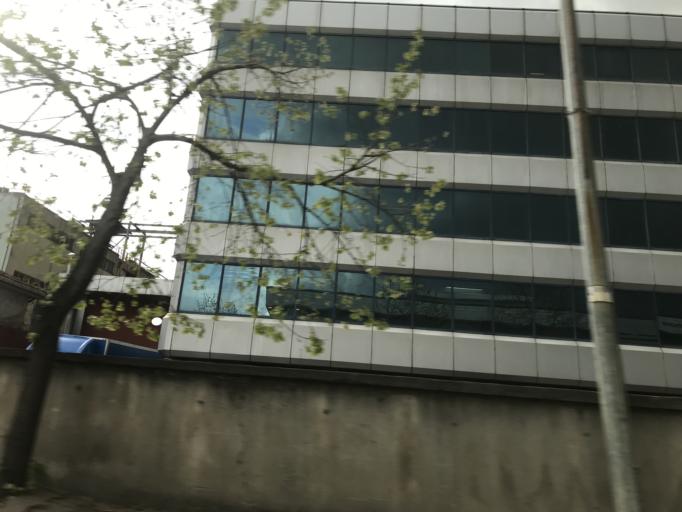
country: TR
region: Istanbul
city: Samandira
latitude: 40.9975
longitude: 29.1786
